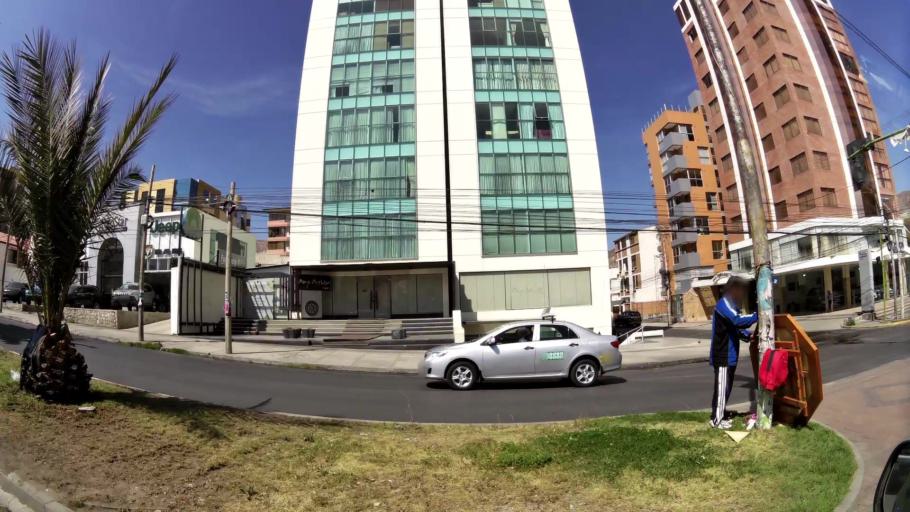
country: BO
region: La Paz
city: La Paz
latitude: -16.5400
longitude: -68.0872
